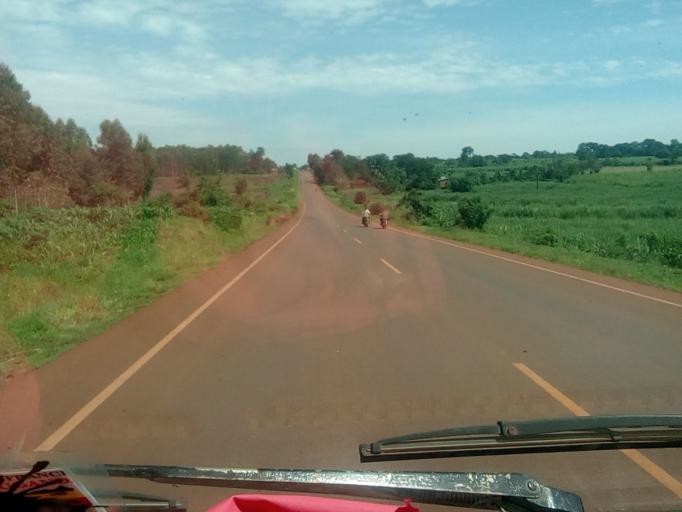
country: UG
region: Eastern Region
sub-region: Jinja District
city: Buwenge
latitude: 0.5668
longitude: 33.2123
